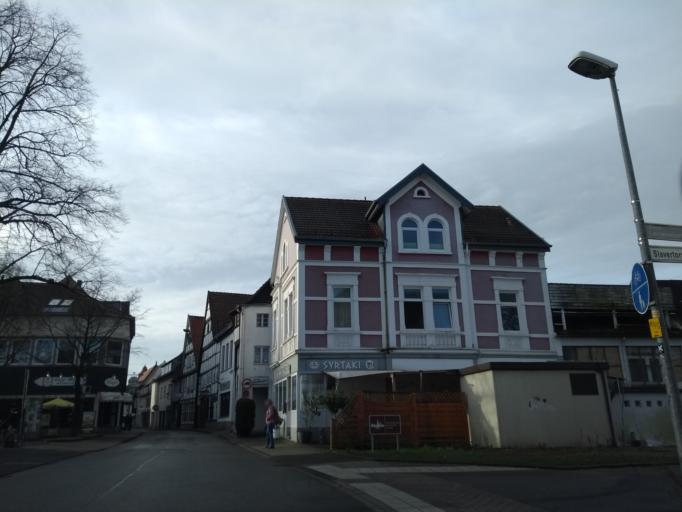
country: DE
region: North Rhine-Westphalia
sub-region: Regierungsbezirk Detmold
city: Lemgo
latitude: 52.0301
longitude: 8.9009
